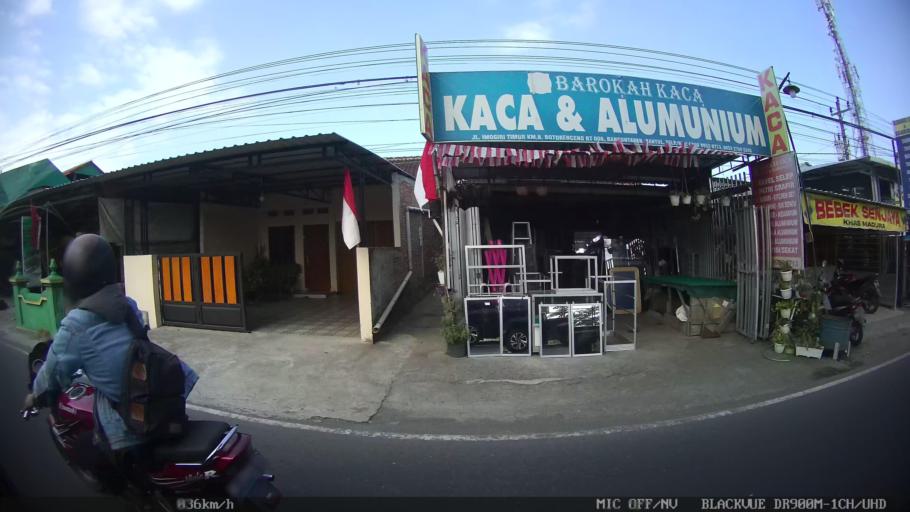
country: ID
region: Daerah Istimewa Yogyakarta
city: Sewon
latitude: -7.8525
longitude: 110.3904
